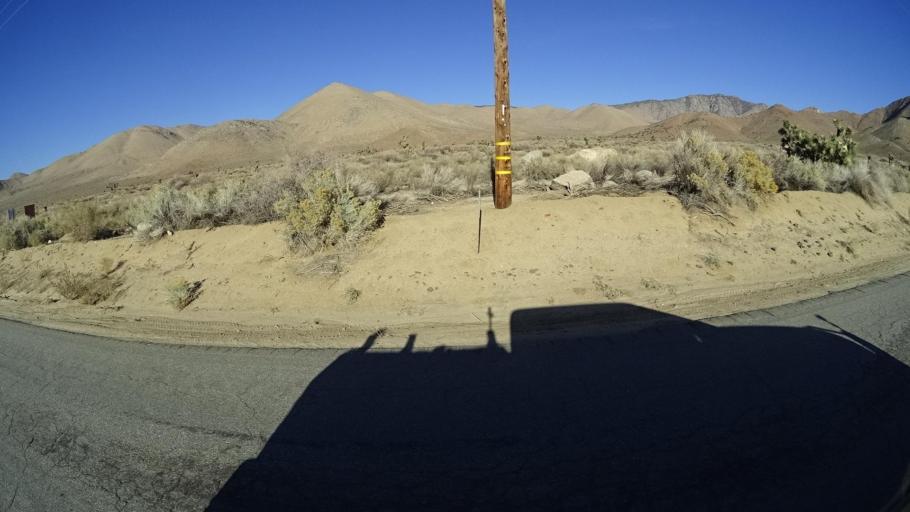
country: US
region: California
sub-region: Kern County
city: Weldon
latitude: 35.5491
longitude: -118.2069
